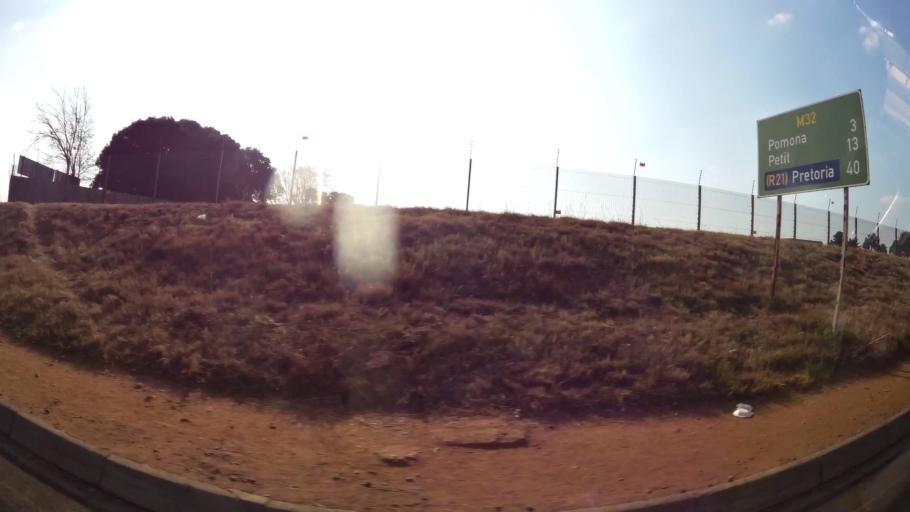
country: ZA
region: Gauteng
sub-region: City of Johannesburg Metropolitan Municipality
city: Modderfontein
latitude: -26.0992
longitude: 28.2540
